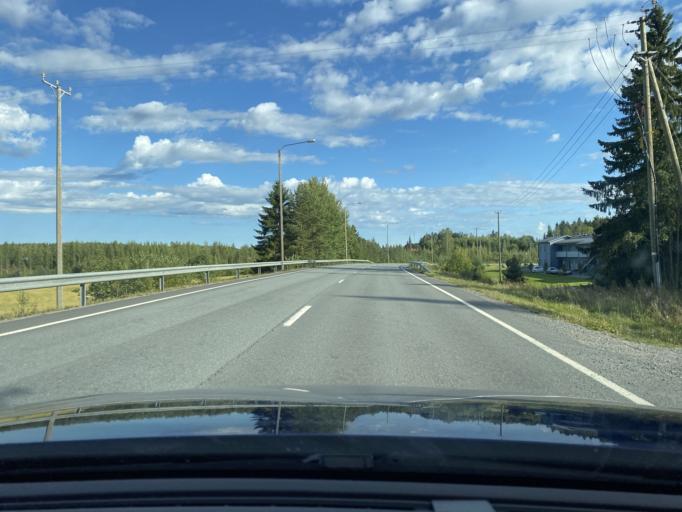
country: FI
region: Pirkanmaa
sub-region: Tampere
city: Lempaeaelae
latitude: 61.3761
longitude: 23.7850
